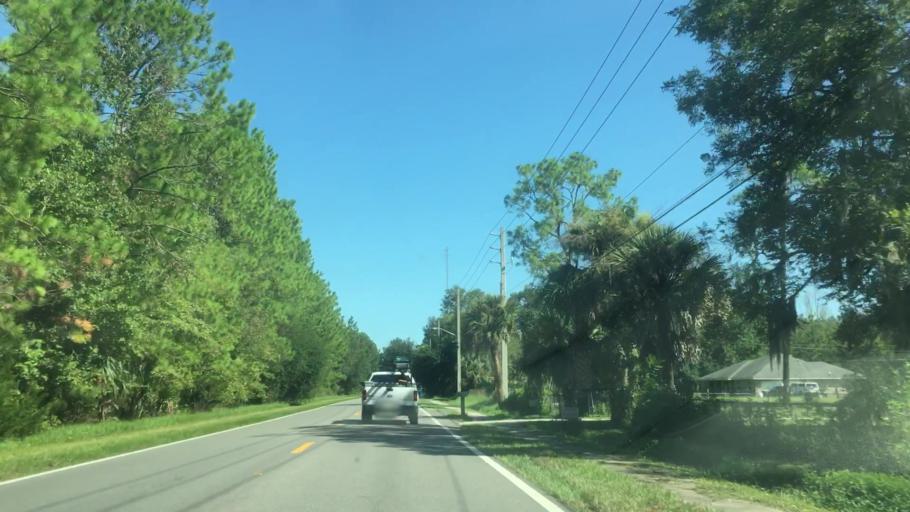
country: US
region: Florida
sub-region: Nassau County
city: Yulee
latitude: 30.4944
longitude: -81.5880
